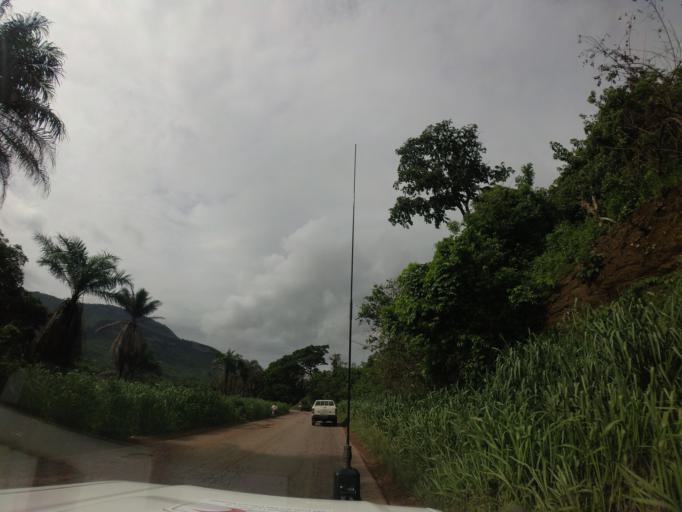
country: GN
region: Kindia
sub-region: Coyah
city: Coyah
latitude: 9.7327
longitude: -13.3731
